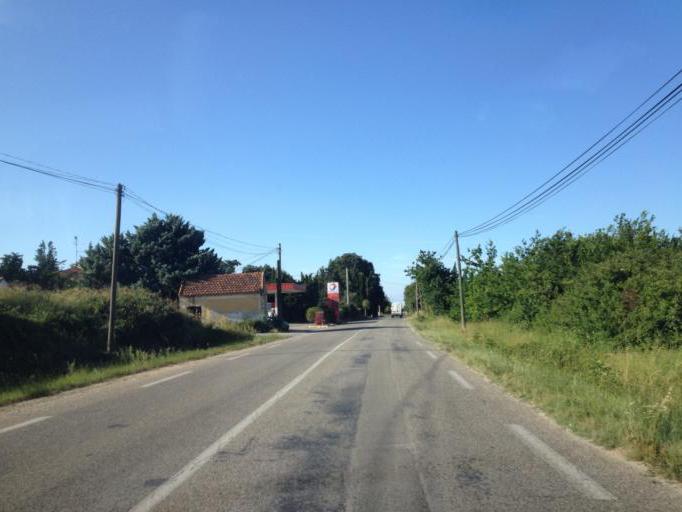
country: FR
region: Provence-Alpes-Cote d'Azur
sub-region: Departement du Vaucluse
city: Orange
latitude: 44.1093
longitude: 4.7921
